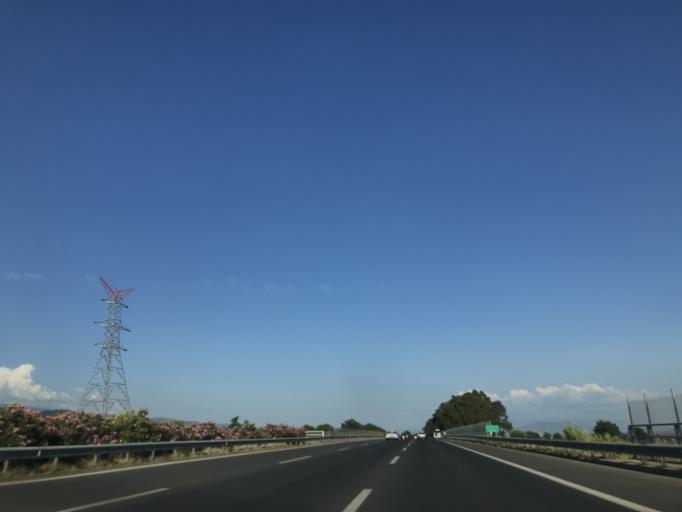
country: TR
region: Aydin
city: Germencik
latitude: 37.8729
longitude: 27.6261
